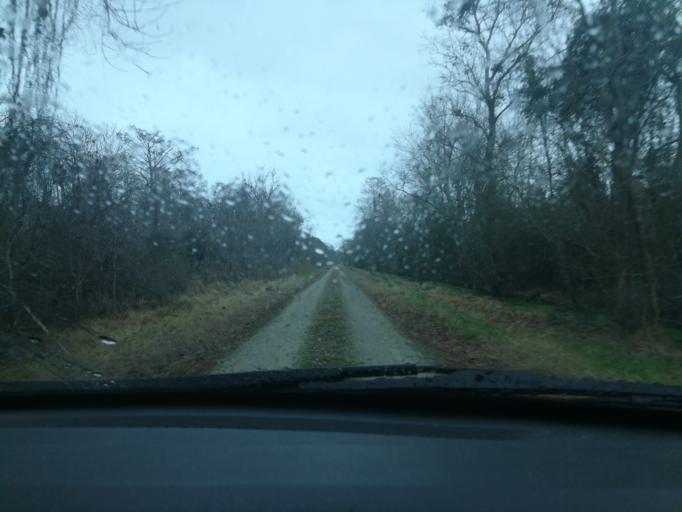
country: US
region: North Carolina
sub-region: Hyde County
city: Swanquarter
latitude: 35.4744
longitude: -76.1322
